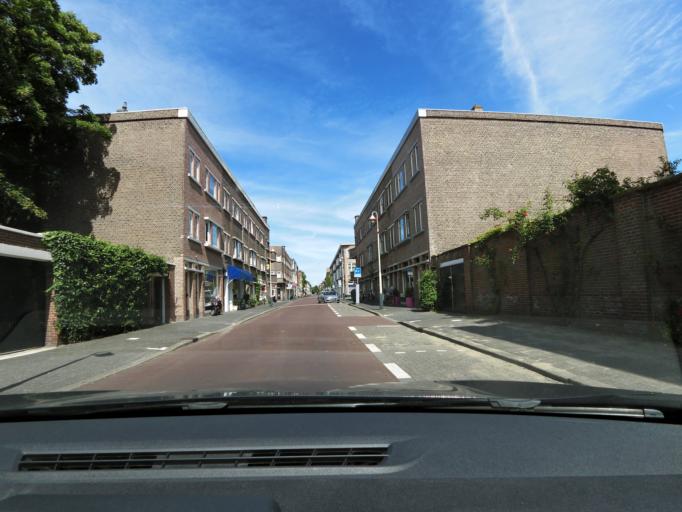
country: NL
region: South Holland
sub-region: Gemeente Den Haag
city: The Hague
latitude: 52.0892
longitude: 4.3176
